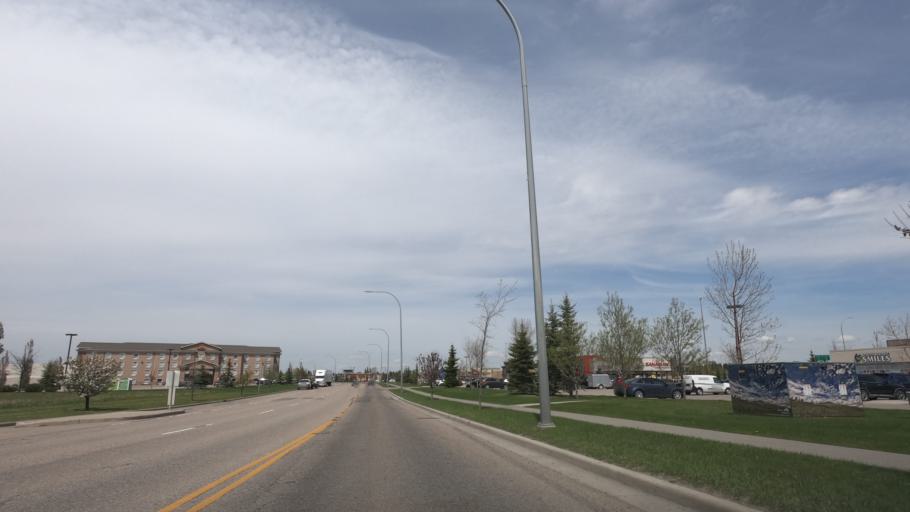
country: CA
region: Alberta
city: Airdrie
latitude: 51.2668
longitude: -114.0036
